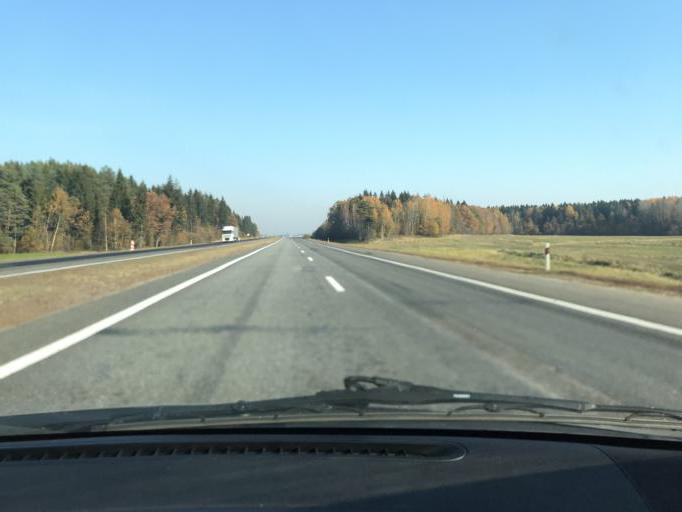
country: BY
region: Vitebsk
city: Horad Orsha
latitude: 54.5853
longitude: 30.3368
